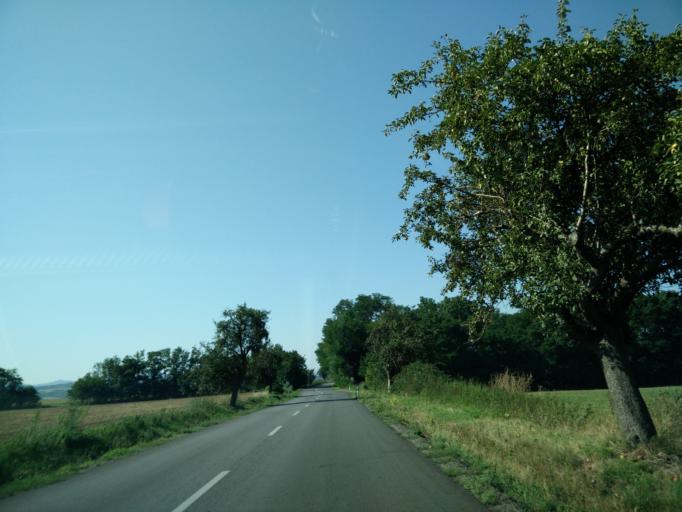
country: SK
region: Nitriansky
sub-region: Okres Nitra
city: Nitra
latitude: 48.4415
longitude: 18.1379
